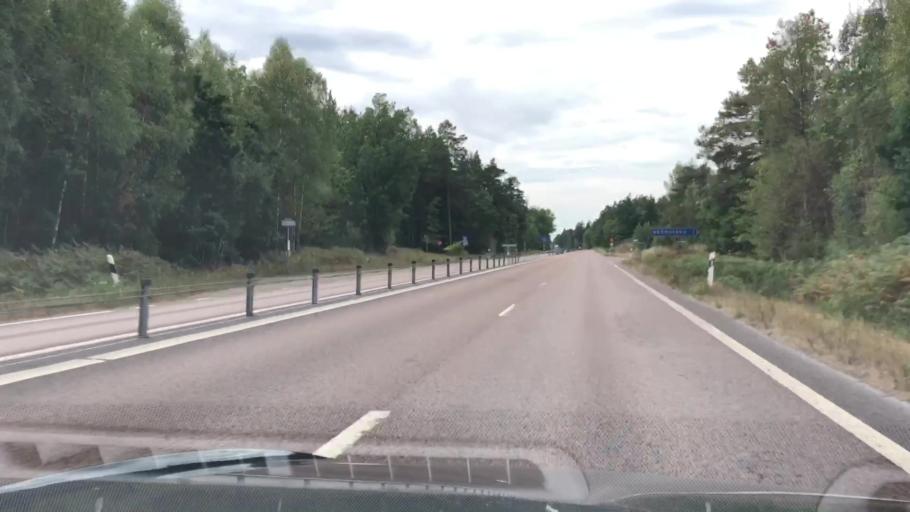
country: SE
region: Kalmar
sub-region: Torsas Kommun
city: Torsas
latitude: 56.2899
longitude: 15.9887
